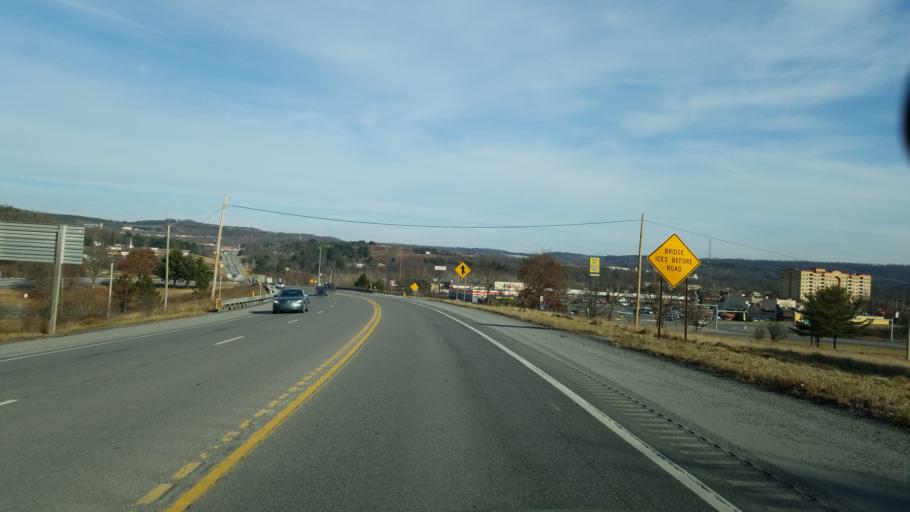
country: US
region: Pennsylvania
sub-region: Clearfield County
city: Clearfield
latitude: 41.0226
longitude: -78.4184
